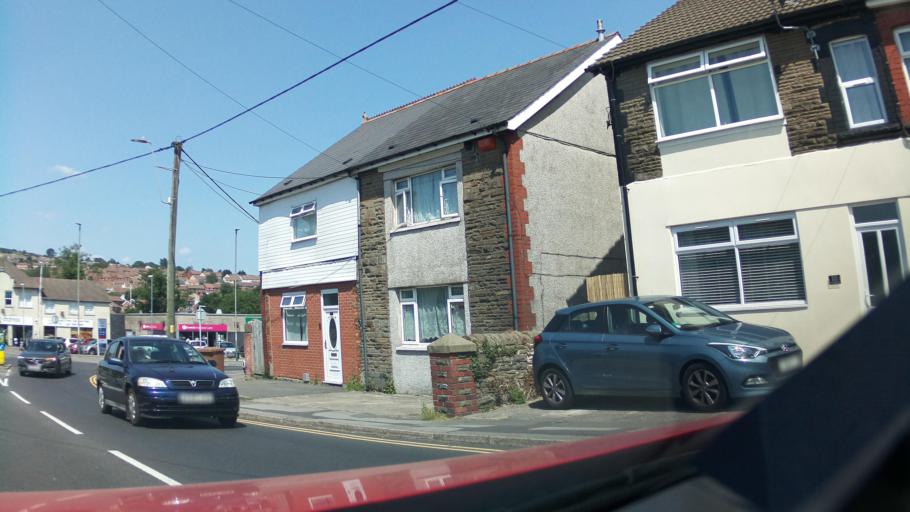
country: GB
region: Wales
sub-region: Caerphilly County Borough
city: Llanbradach
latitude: 51.5844
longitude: -3.2422
